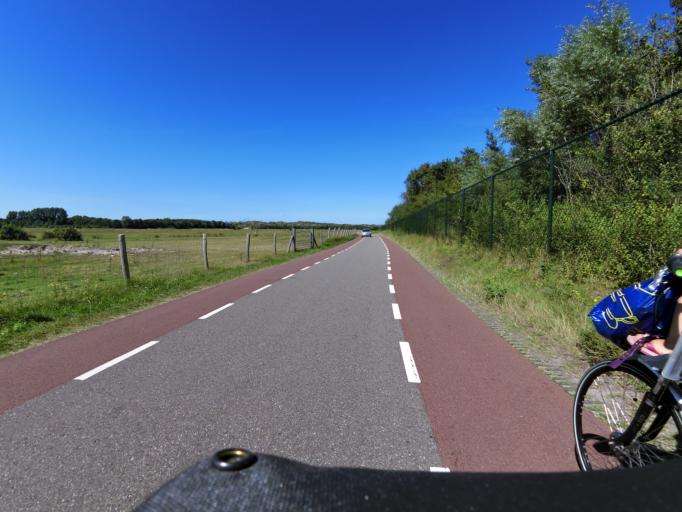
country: NL
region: Zeeland
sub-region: Schouwen-Duiveland
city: Haamstede
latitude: 51.7149
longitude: 3.7222
